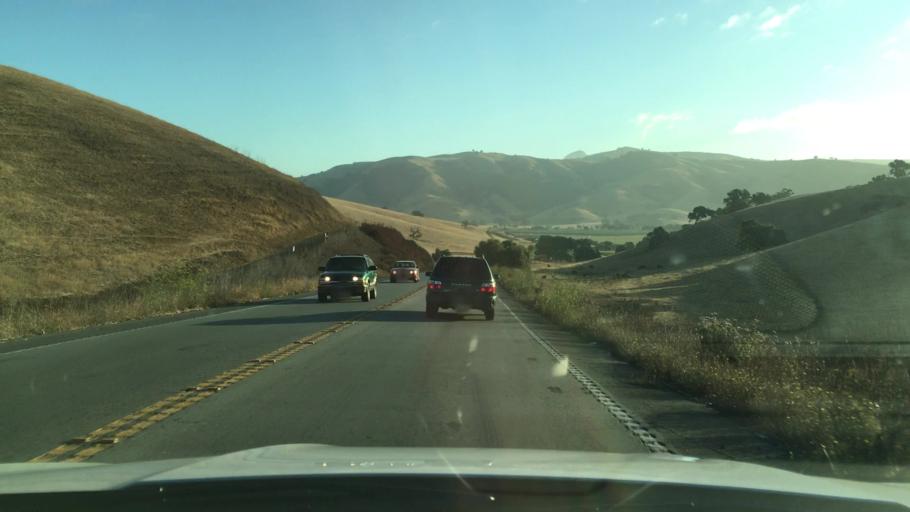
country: US
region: California
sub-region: San Benito County
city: Hollister
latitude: 36.9638
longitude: -121.3951
